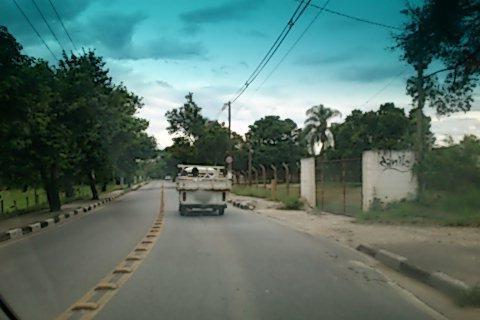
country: BR
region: Sao Paulo
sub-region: Jacarei
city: Jacarei
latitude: -23.2778
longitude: -45.9733
